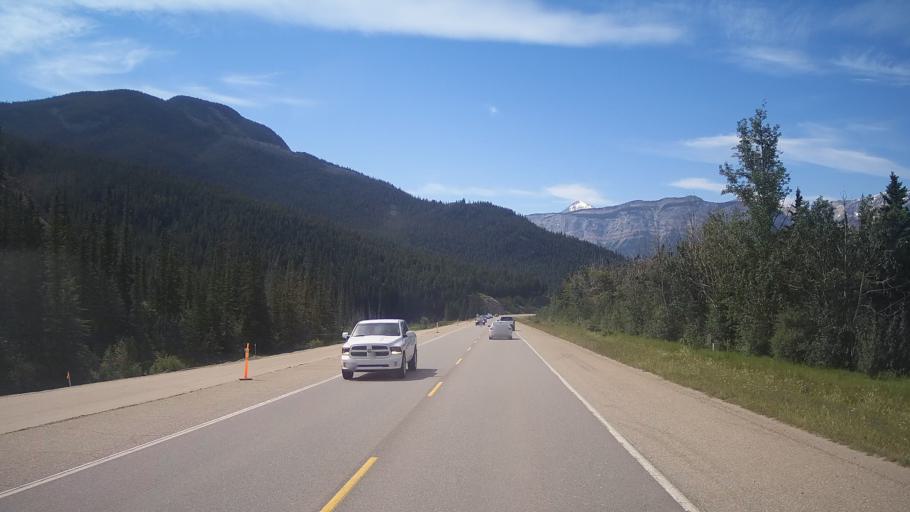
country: CA
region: Alberta
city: Jasper Park Lodge
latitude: 53.0570
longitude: -118.0690
